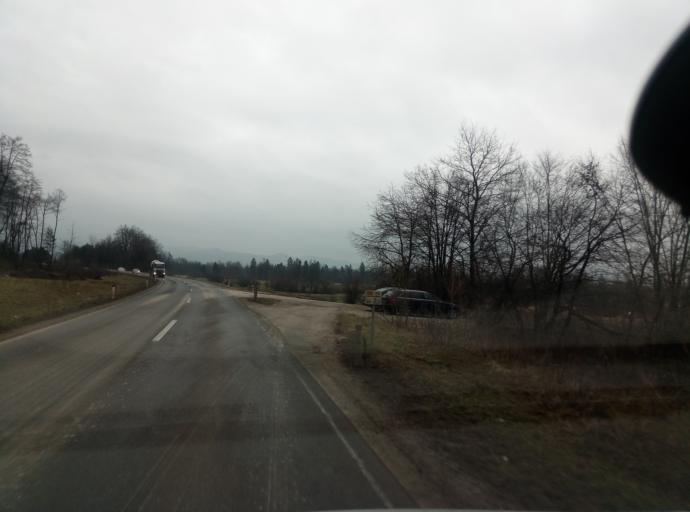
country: SI
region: Dol pri Ljubljani
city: Dol pri Ljubljani
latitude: 46.0934
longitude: 14.5628
